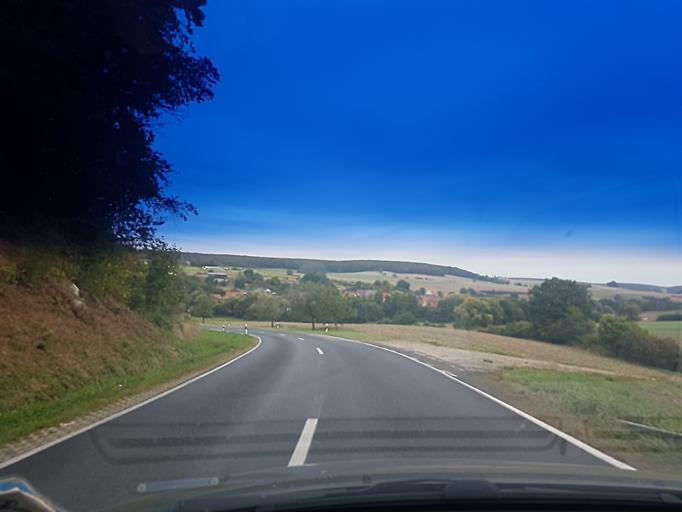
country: DE
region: Bavaria
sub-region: Upper Franconia
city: Burgwindheim
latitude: 49.8763
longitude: 10.5954
